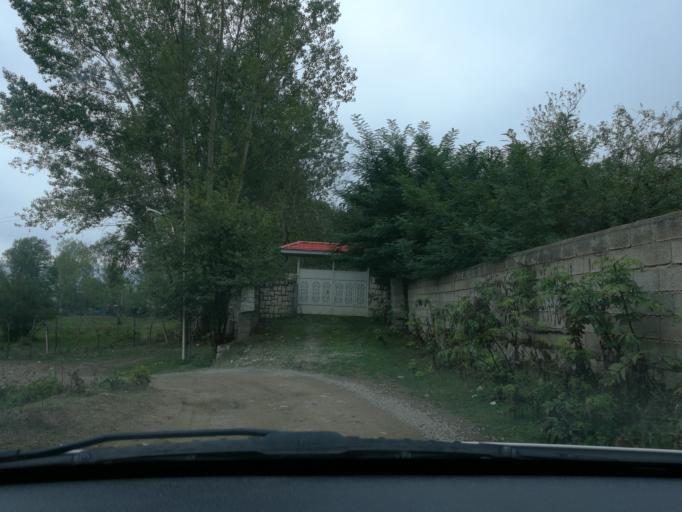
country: IR
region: Mazandaran
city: `Abbasabad
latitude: 36.5056
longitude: 51.1941
